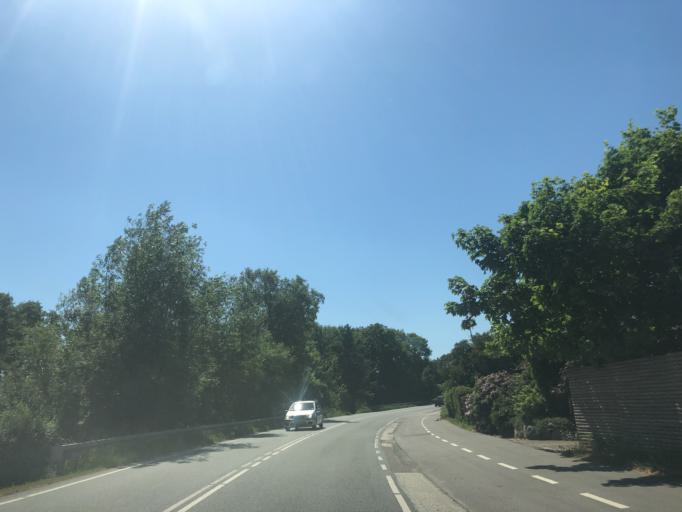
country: DK
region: Capital Region
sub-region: Gribskov Kommune
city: Graested
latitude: 56.0570
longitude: 12.2697
